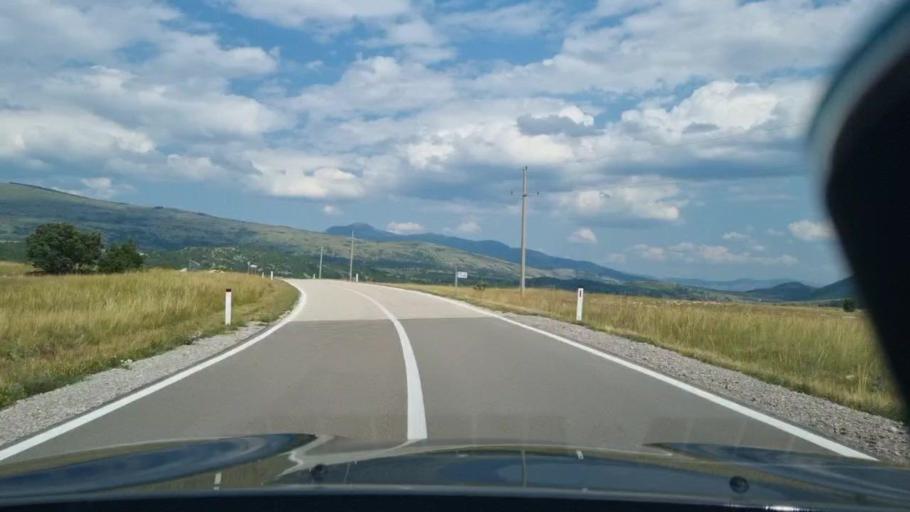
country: BA
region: Federation of Bosnia and Herzegovina
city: Bosansko Grahovo
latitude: 44.1496
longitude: 16.4417
